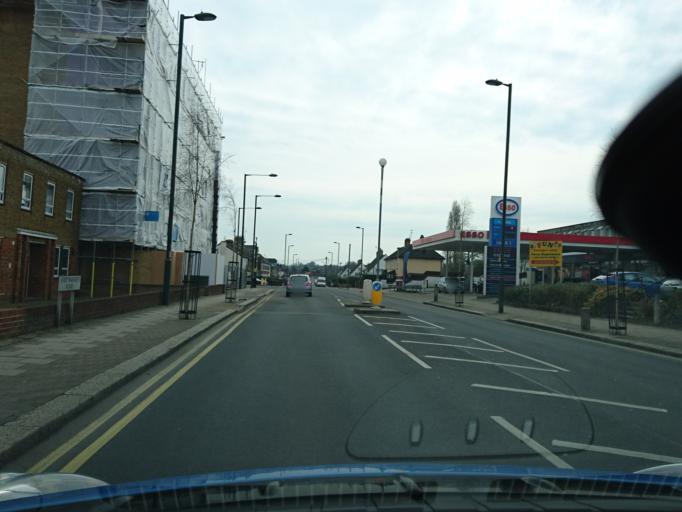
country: GB
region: England
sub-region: Greater London
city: Hadley Wood
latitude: 51.6468
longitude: -0.1669
